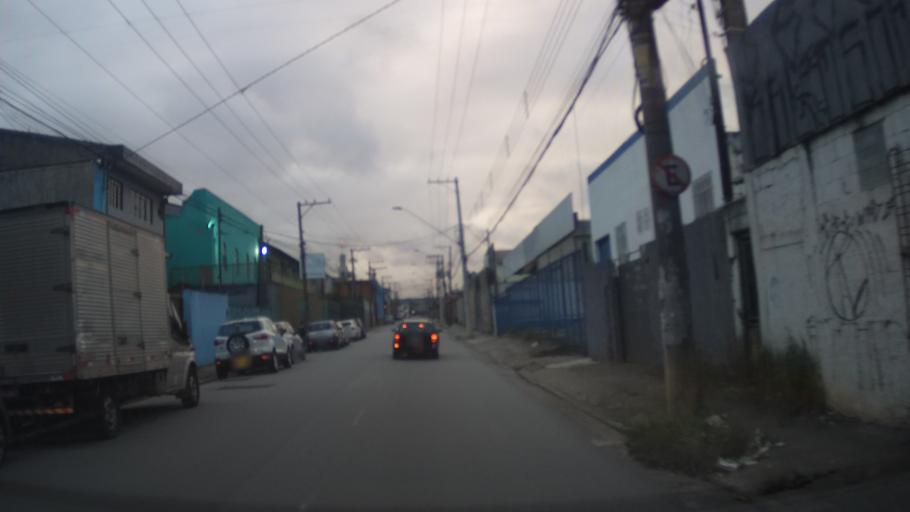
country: BR
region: Sao Paulo
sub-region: Guarulhos
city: Guarulhos
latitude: -23.4566
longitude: -46.4632
